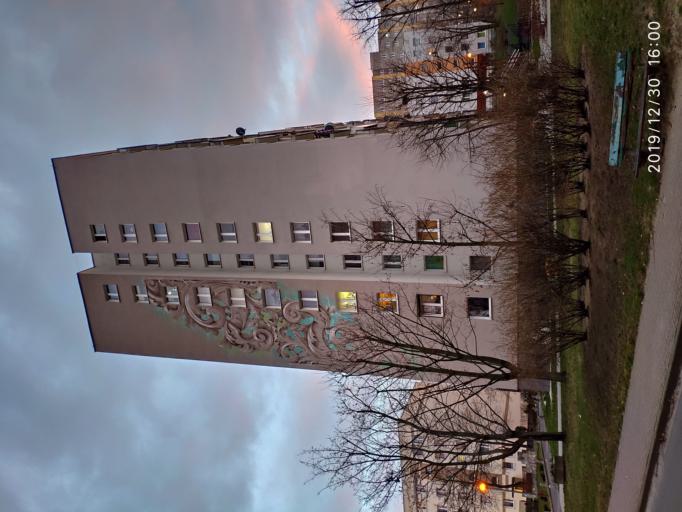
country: PL
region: Lubusz
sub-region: Zielona Gora
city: Zielona Gora
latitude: 51.9378
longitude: 15.4752
